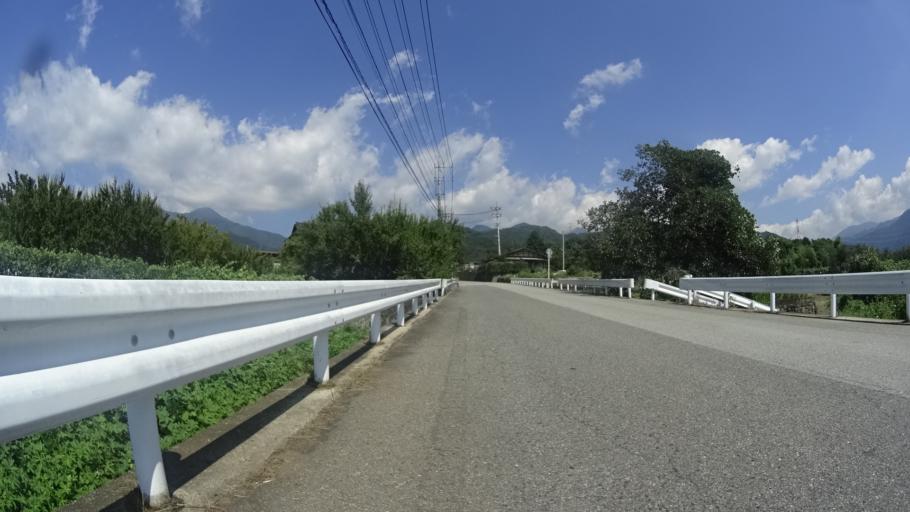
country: JP
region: Yamanashi
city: Enzan
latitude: 35.7481
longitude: 138.7179
